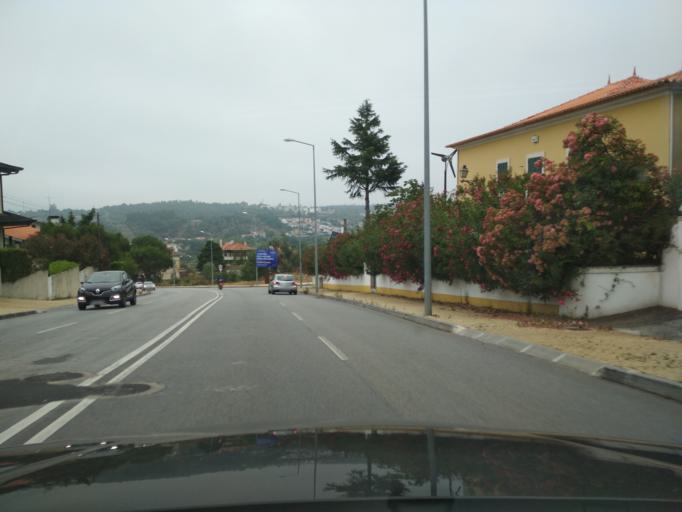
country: PT
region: Coimbra
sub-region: Coimbra
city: Coimbra
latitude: 40.2221
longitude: -8.4078
